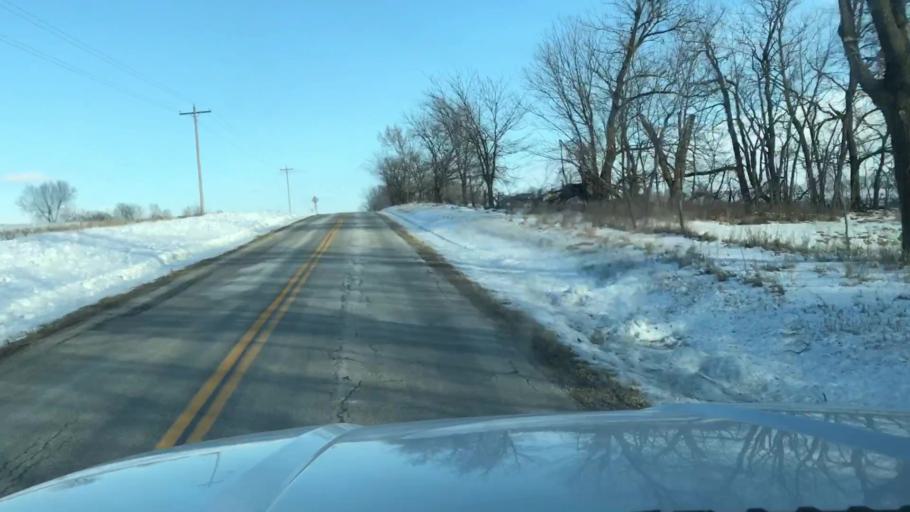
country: US
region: Missouri
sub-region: Holt County
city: Oregon
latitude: 40.1008
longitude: -95.0172
